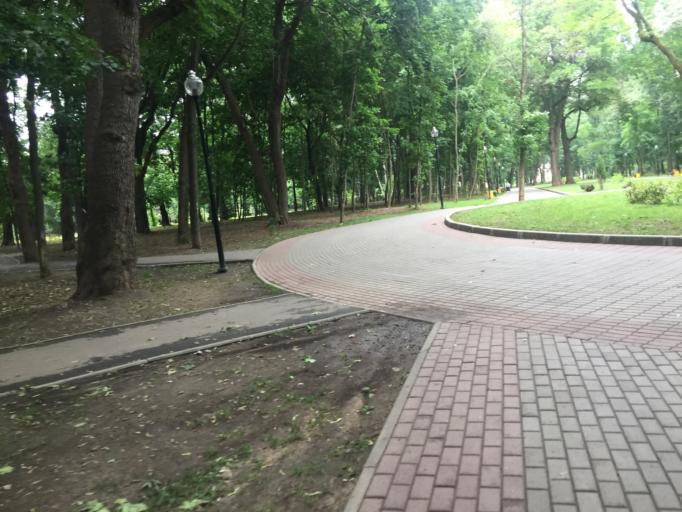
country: RU
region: Tula
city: Tula
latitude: 54.1723
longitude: 37.6158
